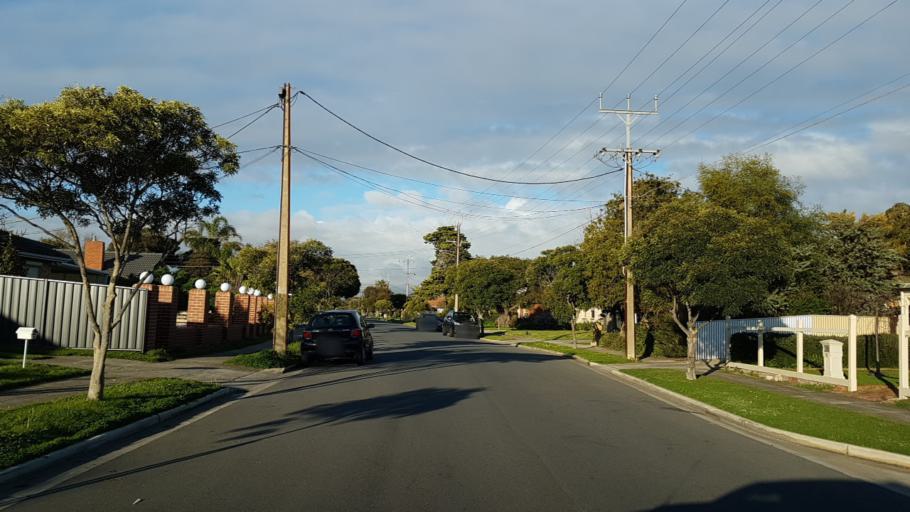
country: AU
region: South Australia
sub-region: Charles Sturt
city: Henley Beach
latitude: -34.9319
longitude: 138.5103
